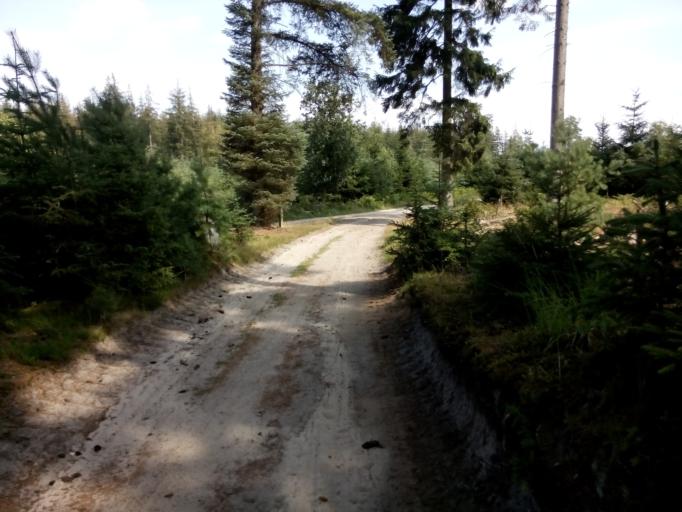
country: DK
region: Central Jutland
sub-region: Skanderborg Kommune
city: Ry
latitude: 56.1042
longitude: 9.7121
